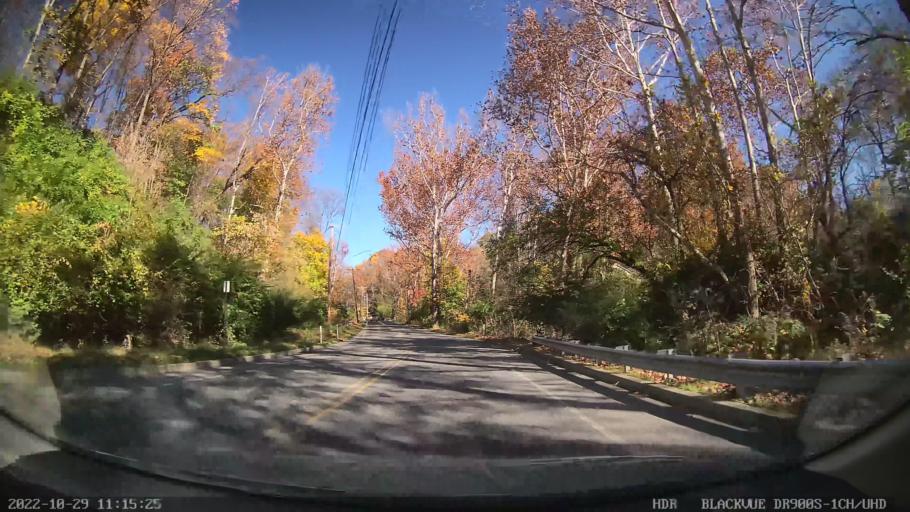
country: US
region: Pennsylvania
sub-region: Northampton County
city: Middletown
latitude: 40.6330
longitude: -75.3349
